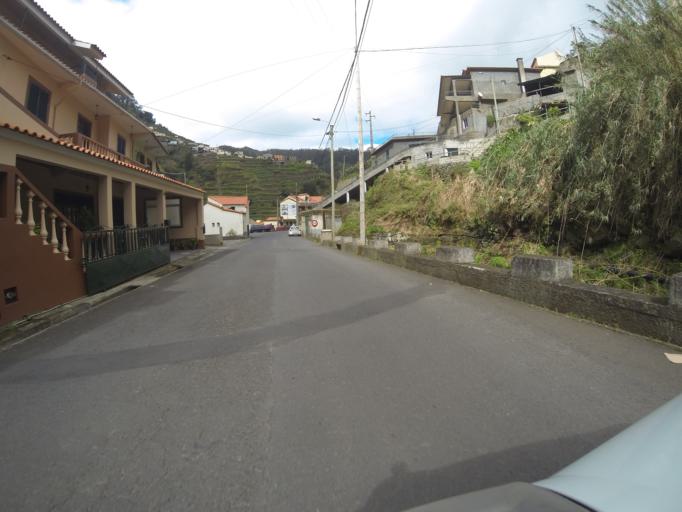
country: PT
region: Madeira
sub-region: Machico
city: Machico
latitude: 32.7357
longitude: -16.7981
